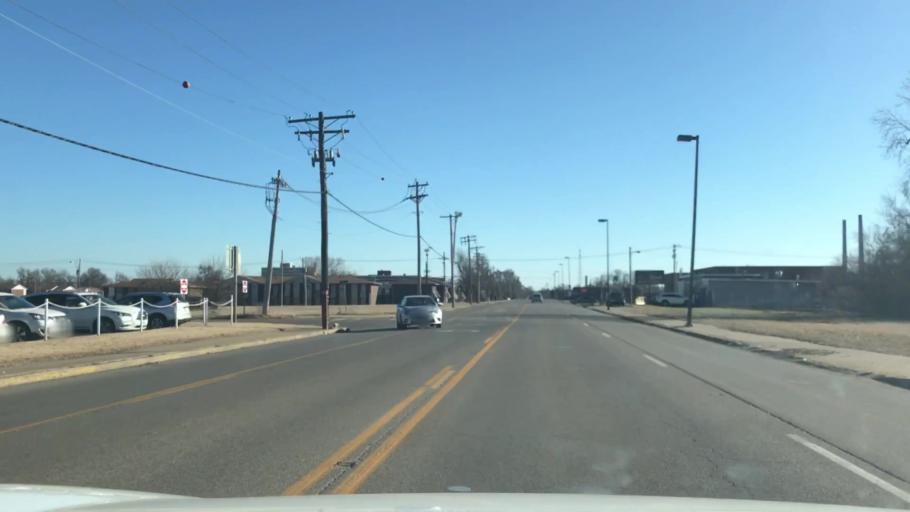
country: US
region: Illinois
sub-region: Saint Clair County
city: East Saint Louis
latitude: 38.6215
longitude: -90.1576
